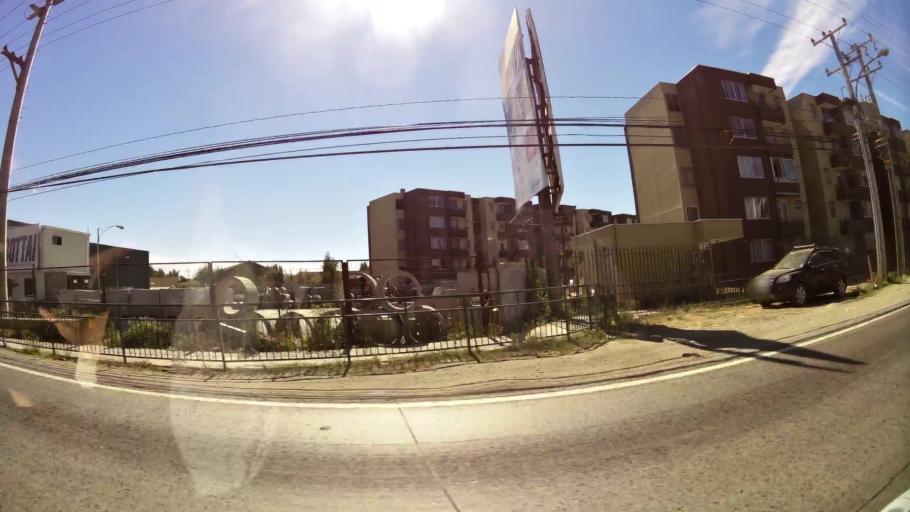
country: CL
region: Biobio
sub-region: Provincia de Concepcion
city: Penco
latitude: -36.7803
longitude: -73.0201
